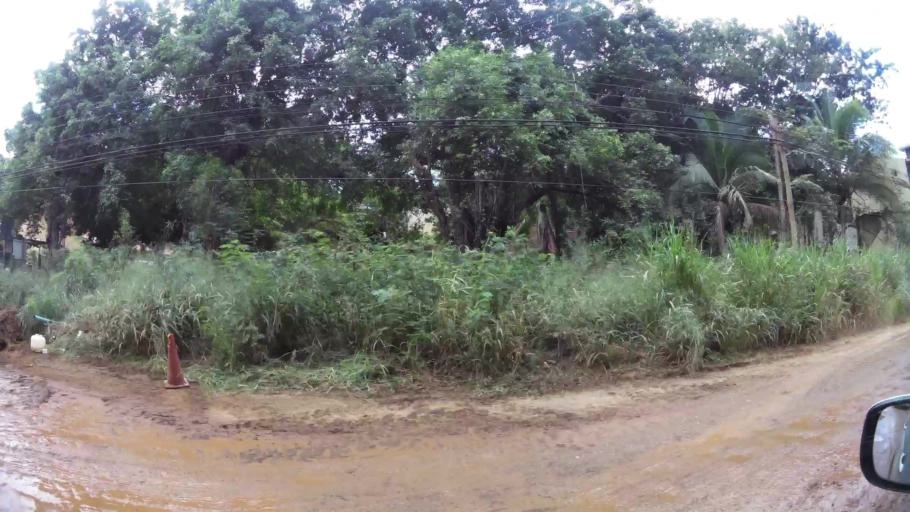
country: CR
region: Guanacaste
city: Santa Cruz
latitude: 10.2966
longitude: -85.8428
